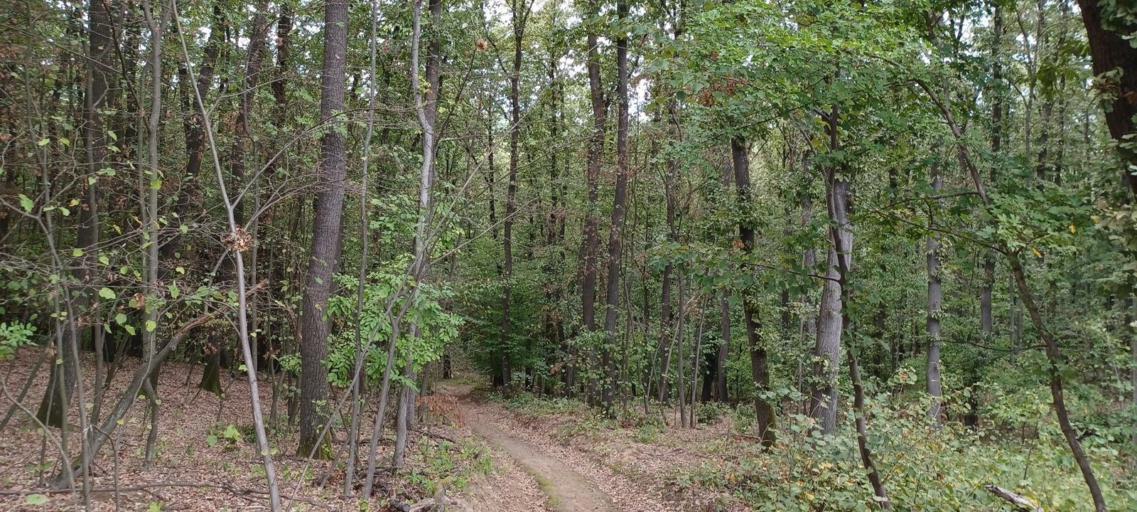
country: HU
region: Tolna
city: Szentgalpuszta
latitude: 46.3388
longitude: 18.6246
